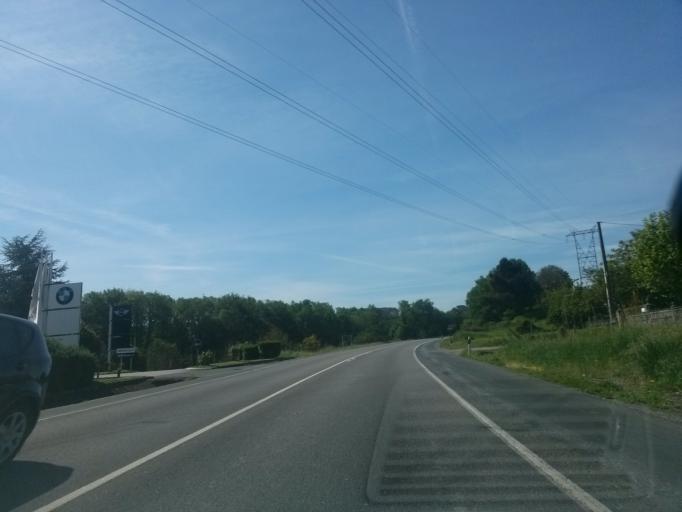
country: ES
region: Galicia
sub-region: Provincia de Lugo
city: Lugo
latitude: 42.9952
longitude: -7.5873
